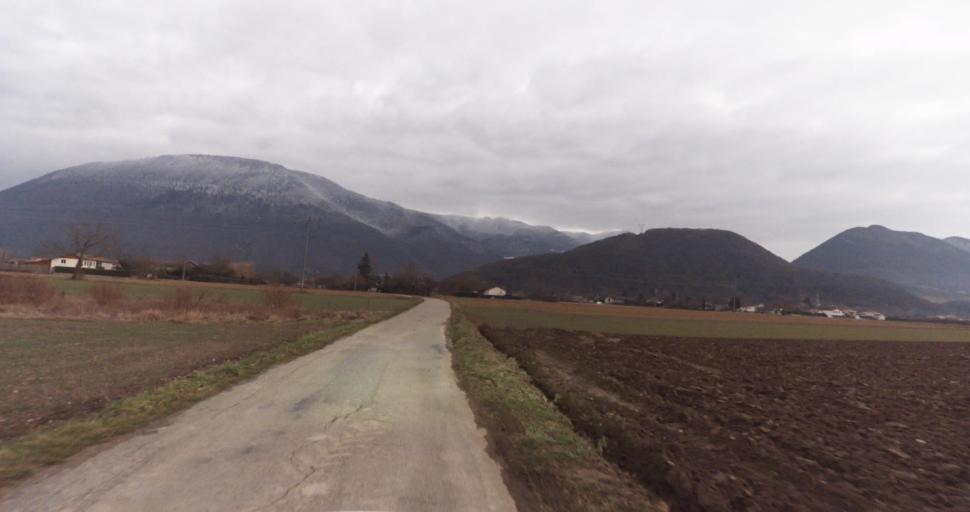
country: FR
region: Rhone-Alpes
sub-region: Departement de l'Isere
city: Vif
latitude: 45.0660
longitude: 5.6861
